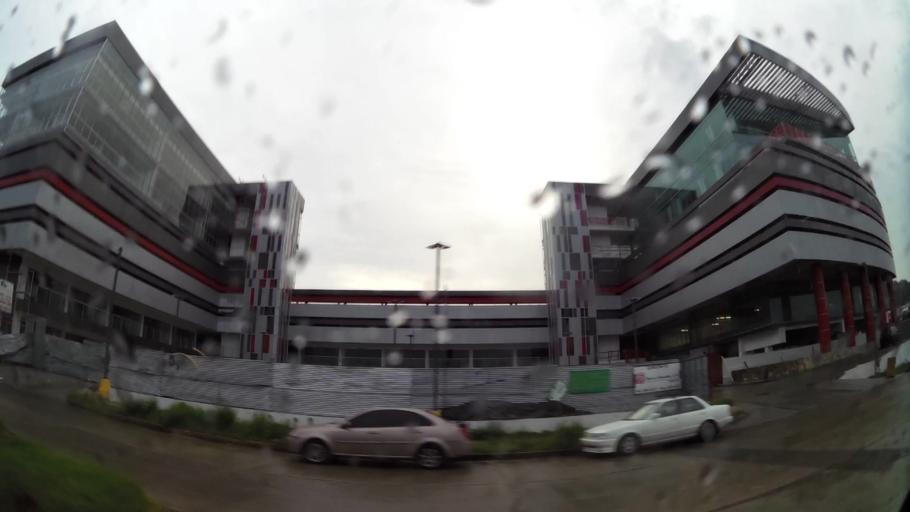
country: PA
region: Panama
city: Panama
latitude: 9.0323
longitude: -79.5324
